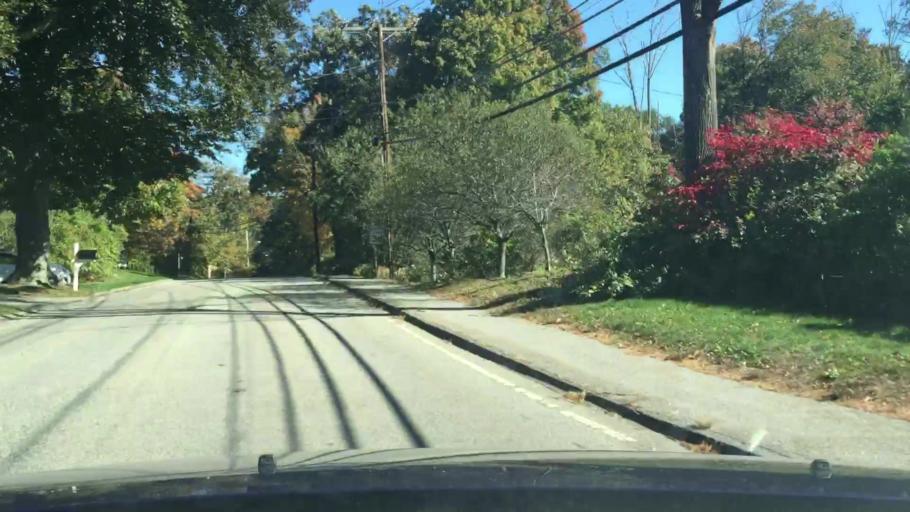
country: US
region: Massachusetts
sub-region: Essex County
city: North Andover
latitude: 42.6816
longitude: -71.0987
